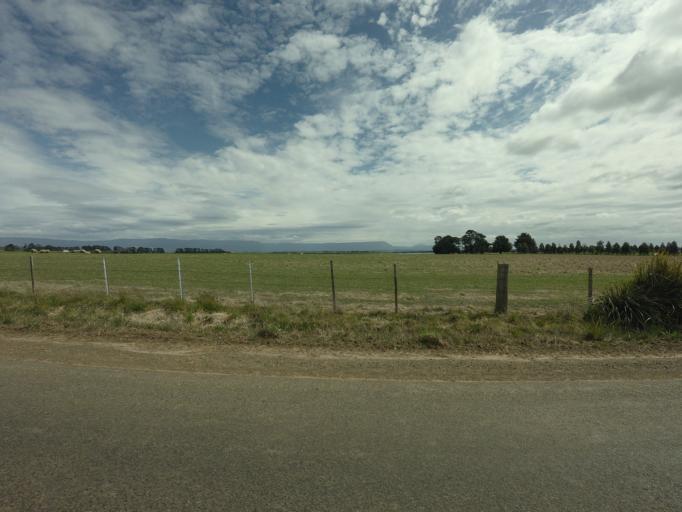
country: AU
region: Tasmania
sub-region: Northern Midlands
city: Longford
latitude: -41.7054
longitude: 147.1966
